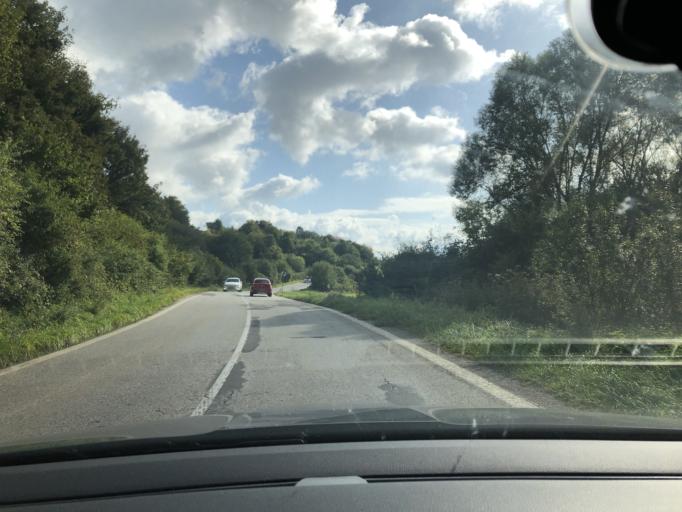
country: SK
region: Zilinsky
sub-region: Okres Dolny Kubin
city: Dolny Kubin
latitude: 49.1994
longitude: 19.1830
